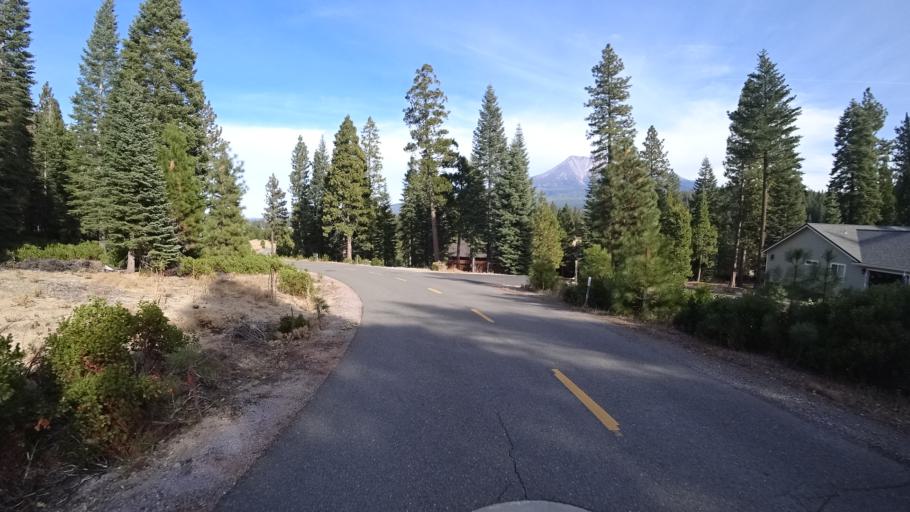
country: US
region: California
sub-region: Siskiyou County
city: Weed
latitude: 41.3927
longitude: -122.3913
